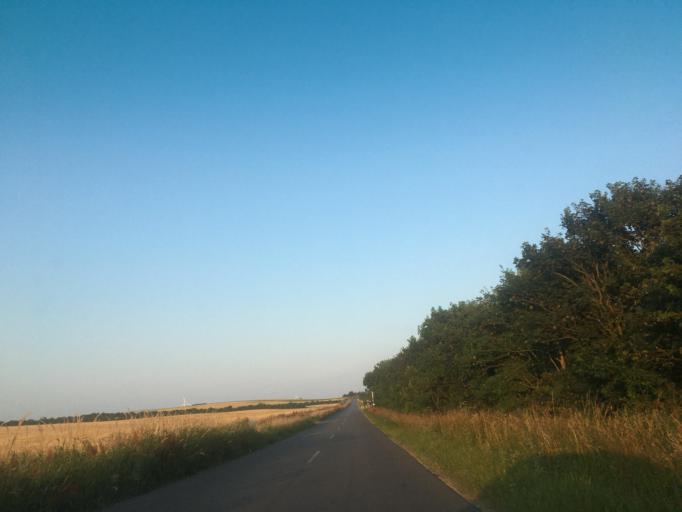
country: DK
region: North Denmark
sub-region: Thisted Kommune
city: Hurup
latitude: 56.7621
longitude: 8.3275
